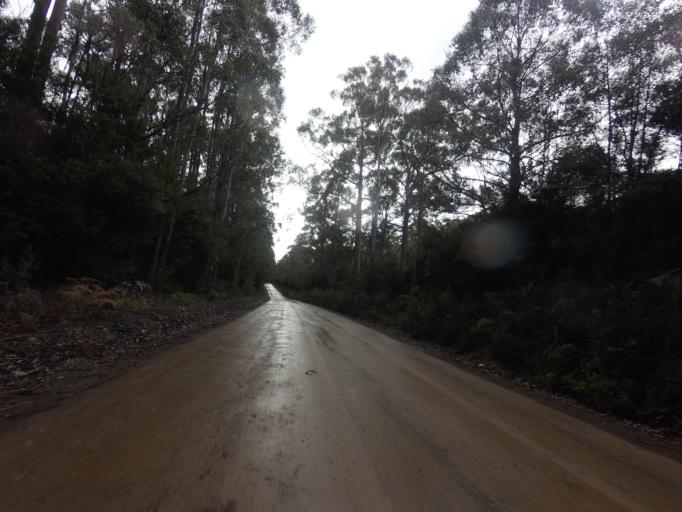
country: AU
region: Tasmania
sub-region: Huon Valley
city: Geeveston
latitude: -43.4571
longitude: 146.9027
